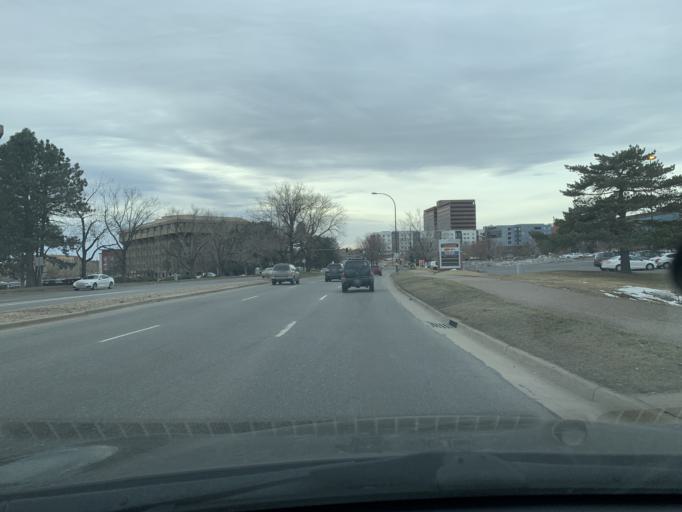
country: US
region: Colorado
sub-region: Jefferson County
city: West Pleasant View
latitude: 39.7177
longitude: -105.1327
